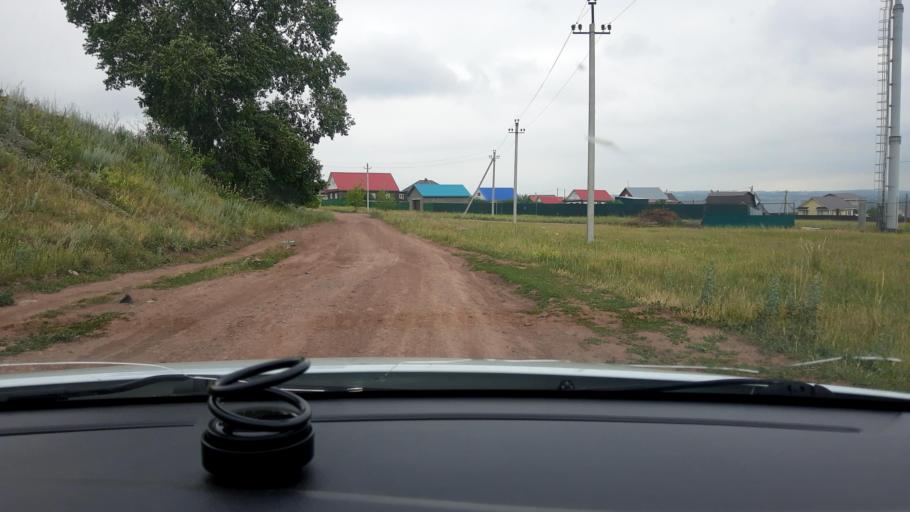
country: RU
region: Bashkortostan
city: Avdon
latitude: 54.6415
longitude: 55.5668
